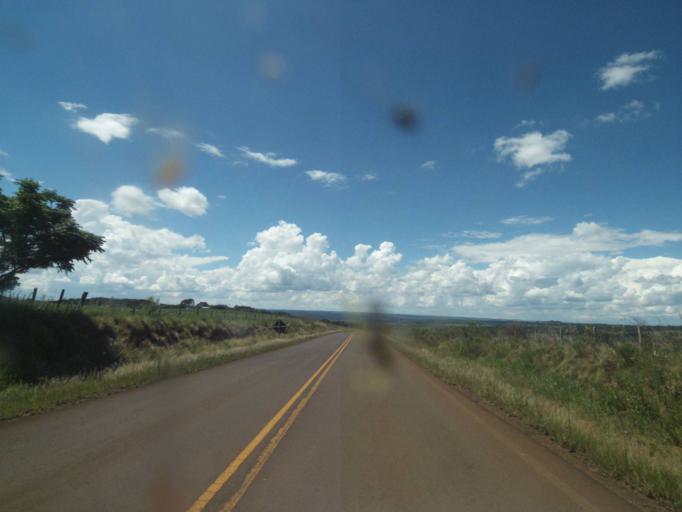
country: BR
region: Parana
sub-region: Pinhao
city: Pinhao
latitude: -25.7987
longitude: -52.0749
